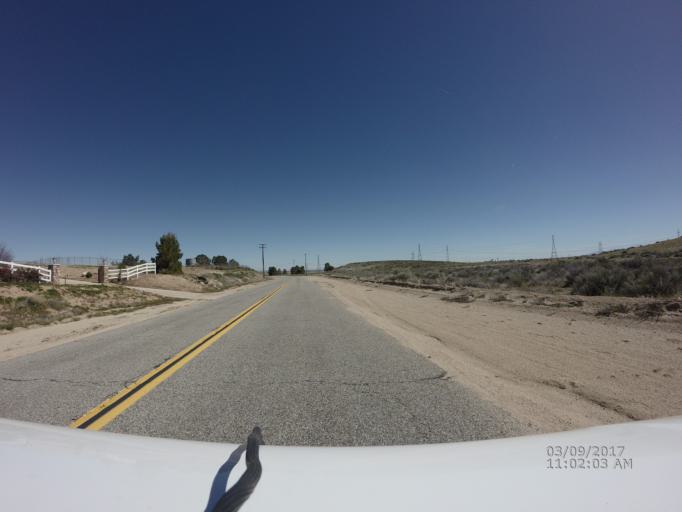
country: US
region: California
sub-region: Los Angeles County
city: Green Valley
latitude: 34.7078
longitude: -118.3578
